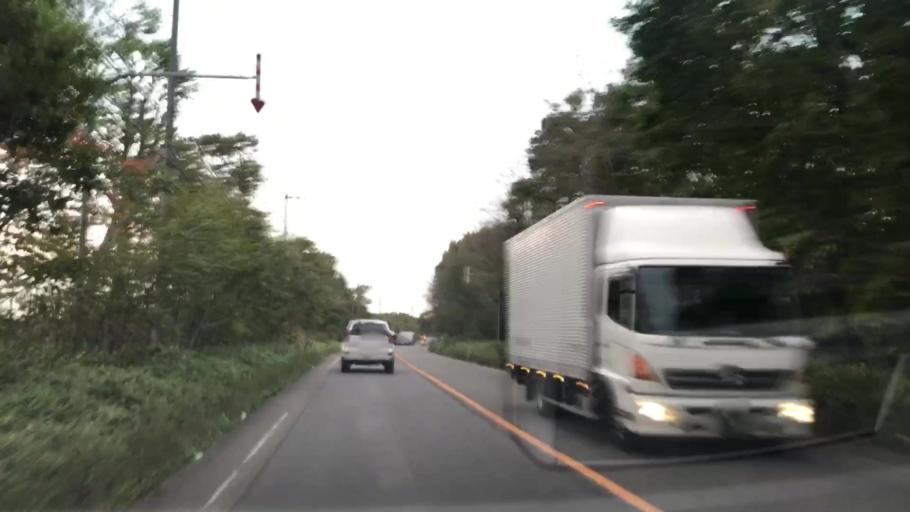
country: JP
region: Hokkaido
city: Tomakomai
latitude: 42.7059
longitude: 141.6638
